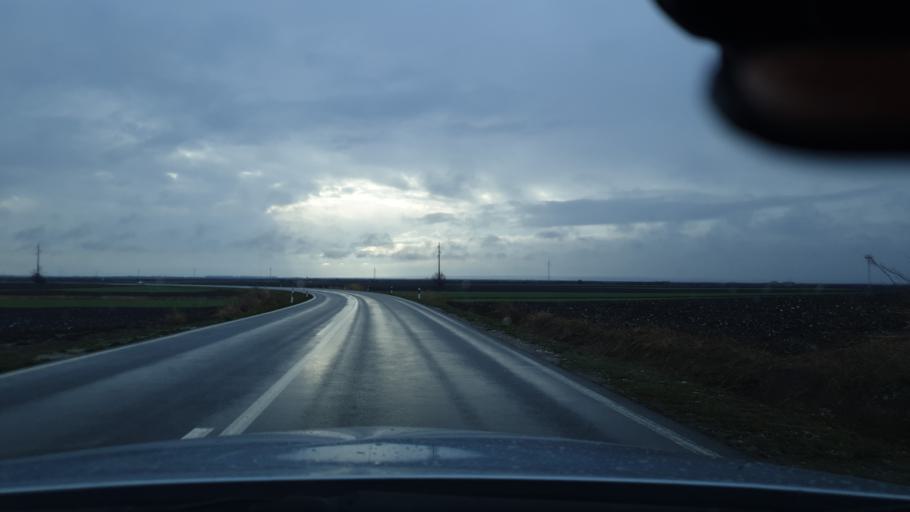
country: RS
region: Autonomna Pokrajina Vojvodina
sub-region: Juznobanatski Okrug
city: Kovin
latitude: 44.8129
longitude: 20.8566
